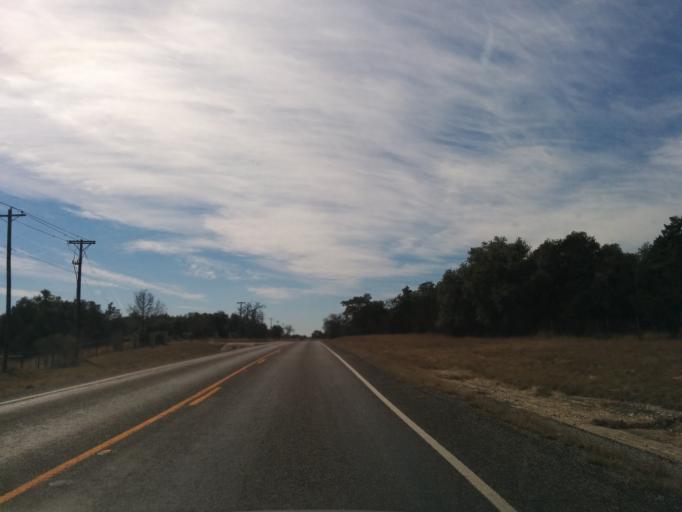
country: US
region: Texas
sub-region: Bexar County
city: Fair Oaks Ranch
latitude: 29.8836
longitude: -98.5567
